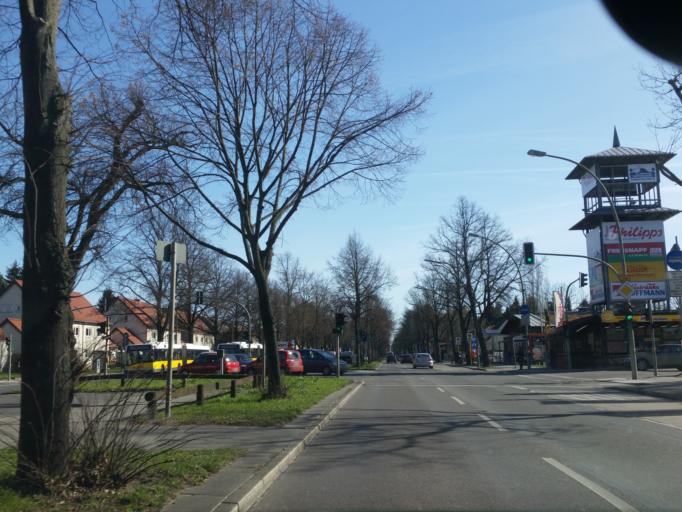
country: DE
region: Berlin
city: Mariendorf
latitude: 52.4270
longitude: 13.3940
